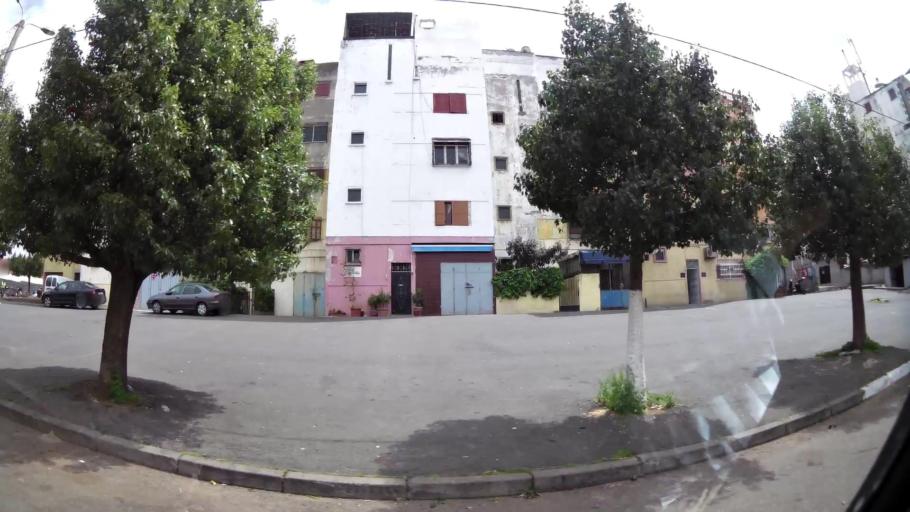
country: MA
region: Grand Casablanca
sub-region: Casablanca
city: Casablanca
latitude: 33.5770
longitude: -7.5612
